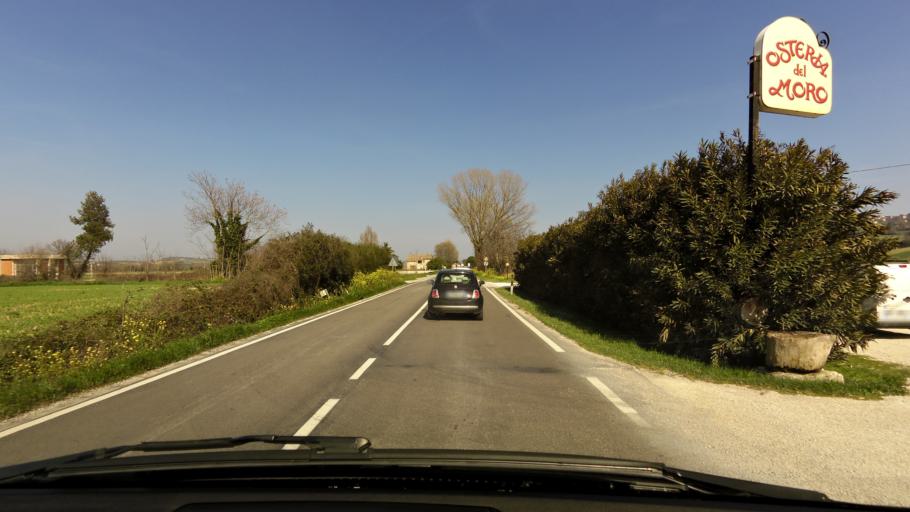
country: IT
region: The Marches
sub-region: Provincia di Macerata
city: Potenza Picena
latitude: 43.3751
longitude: 13.5964
